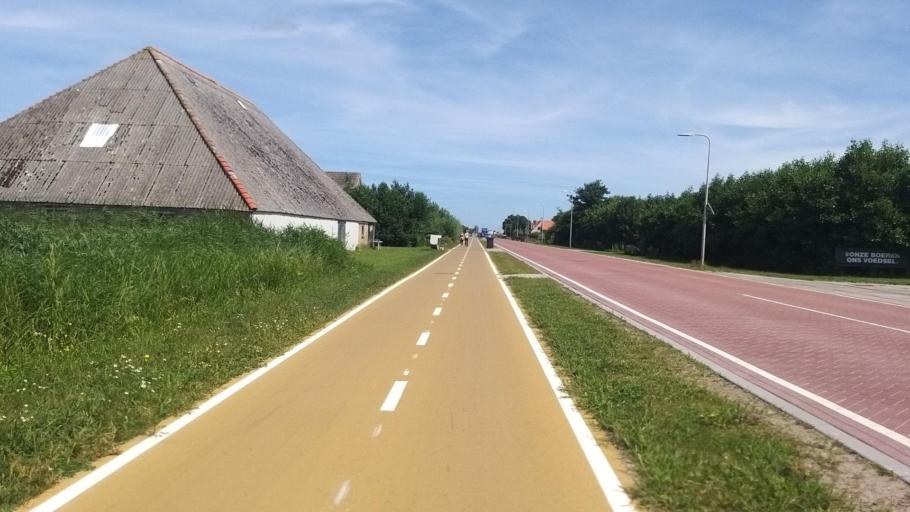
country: NL
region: North Holland
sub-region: Gemeente Texel
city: Den Burg
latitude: 53.1099
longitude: 4.8168
